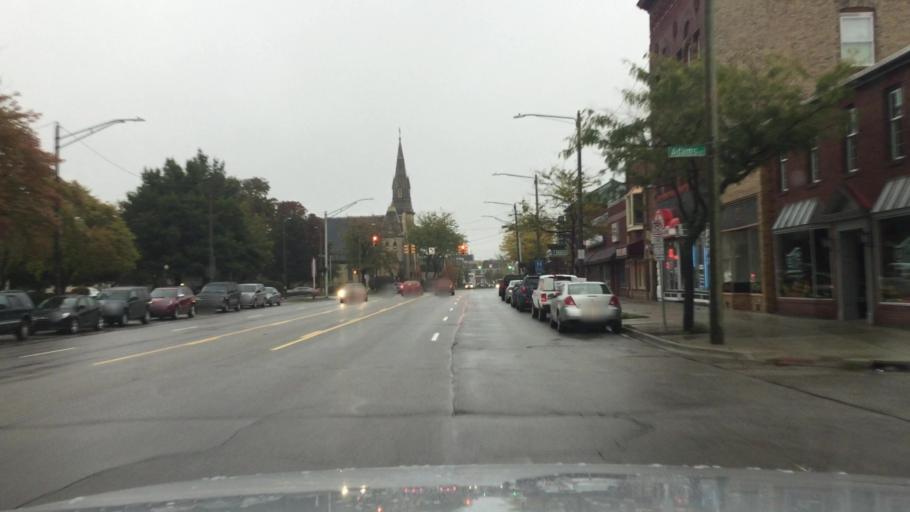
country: US
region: Michigan
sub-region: Saginaw County
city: Saginaw
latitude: 43.4168
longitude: -83.9653
